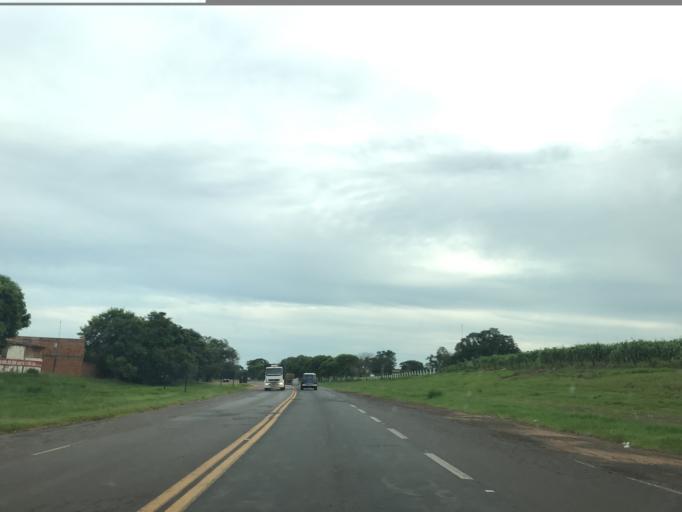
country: BR
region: Sao Paulo
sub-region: Tupa
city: Tupa
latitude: -21.6420
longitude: -50.4996
